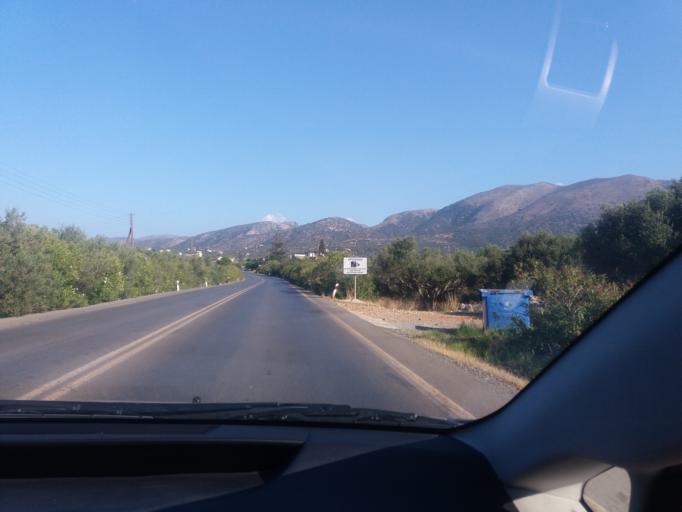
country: GR
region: Crete
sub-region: Nomos Irakleiou
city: Malia
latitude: 35.2897
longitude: 25.4932
